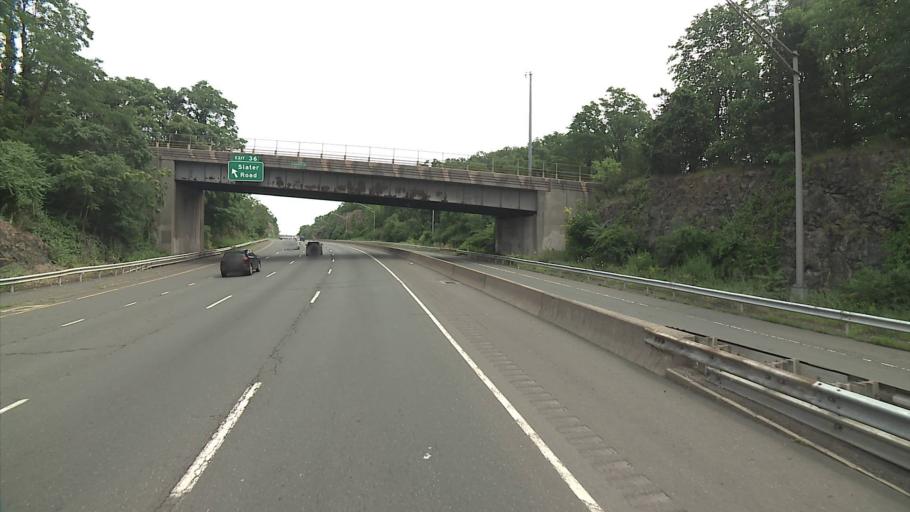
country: US
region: Connecticut
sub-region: Hartford County
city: Plainville
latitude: 41.6706
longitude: -72.8212
